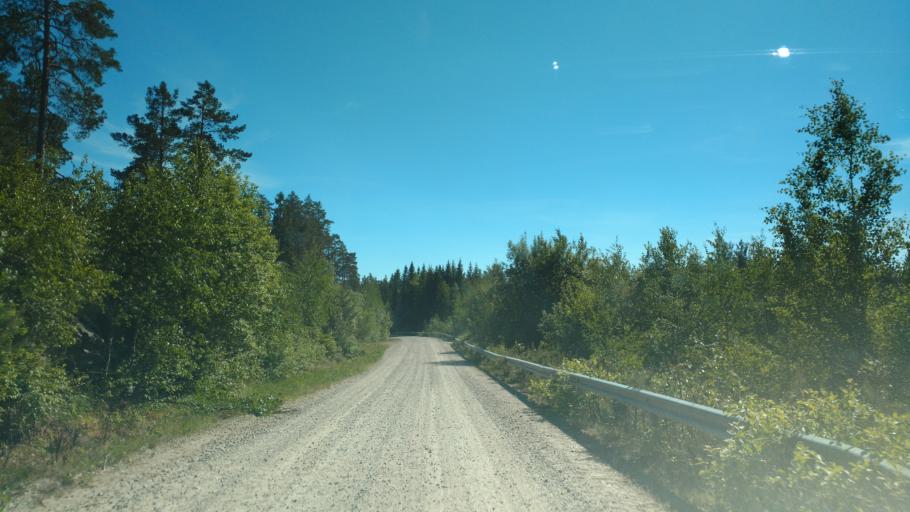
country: FI
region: Varsinais-Suomi
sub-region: Salo
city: Halikko
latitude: 60.4330
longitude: 22.9554
